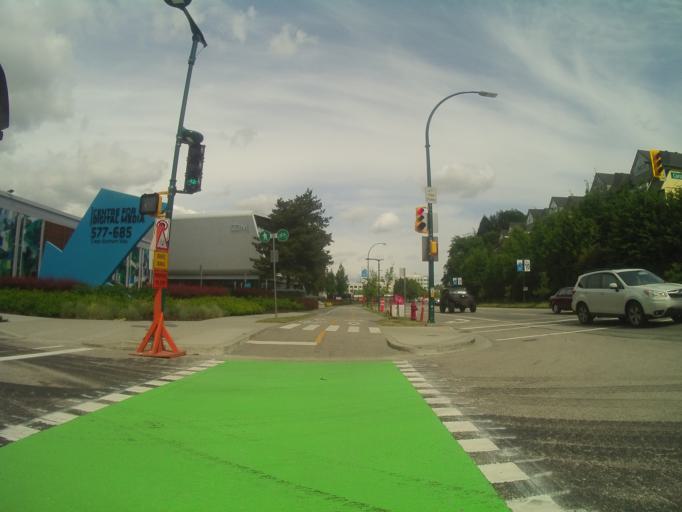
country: CA
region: British Columbia
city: Vancouver
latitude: 49.2669
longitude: -123.0909
